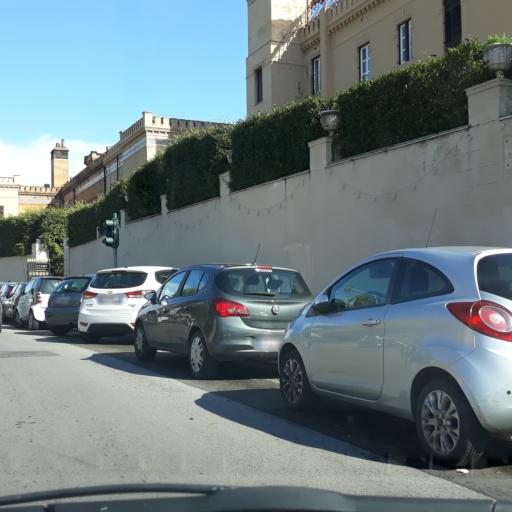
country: IT
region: Sicily
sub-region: Palermo
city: Palermo
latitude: 38.1451
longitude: 13.3695
